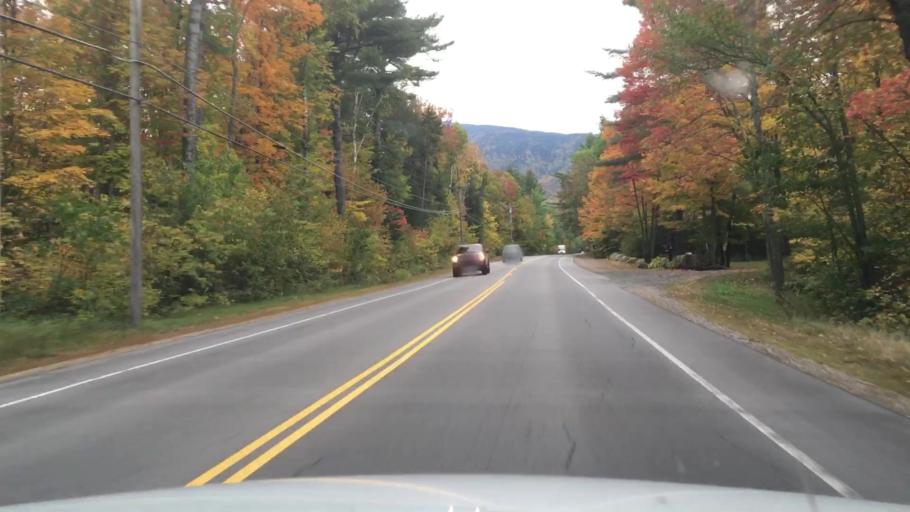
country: US
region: New Hampshire
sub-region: Coos County
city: Gorham
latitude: 44.3728
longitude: -71.1747
